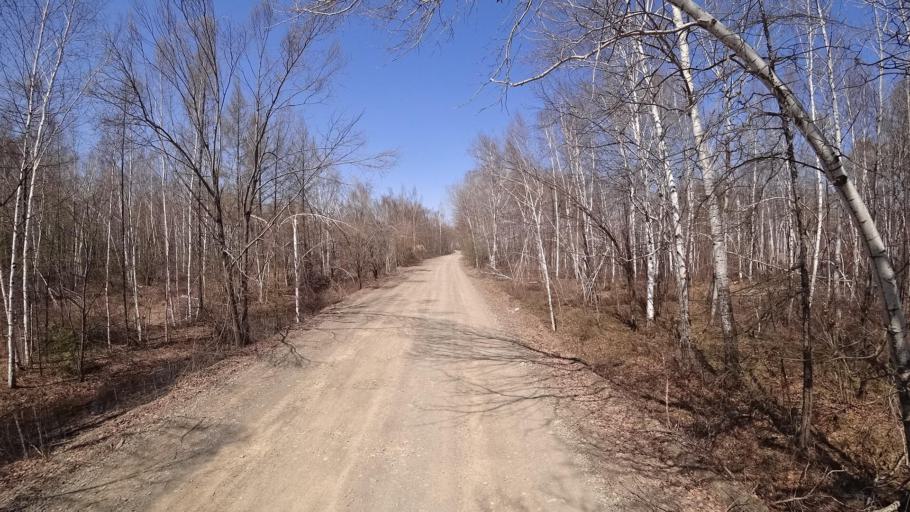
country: RU
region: Khabarovsk Krai
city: Khurba
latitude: 50.4157
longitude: 136.8388
